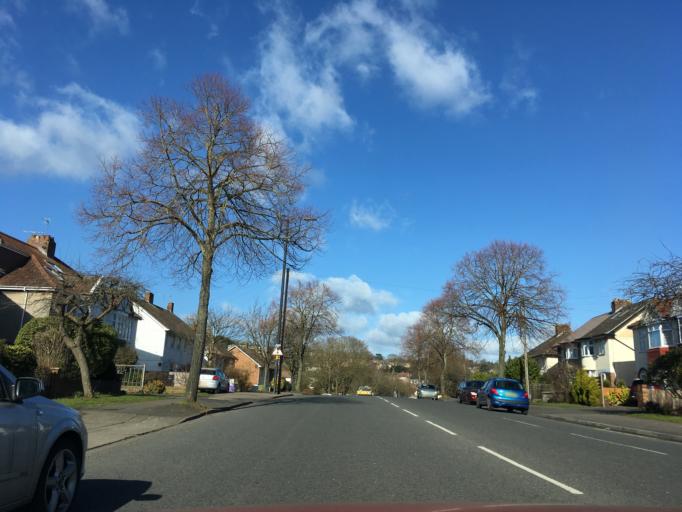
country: GB
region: England
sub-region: Bristol
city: Bristol
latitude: 51.4938
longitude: -2.6220
